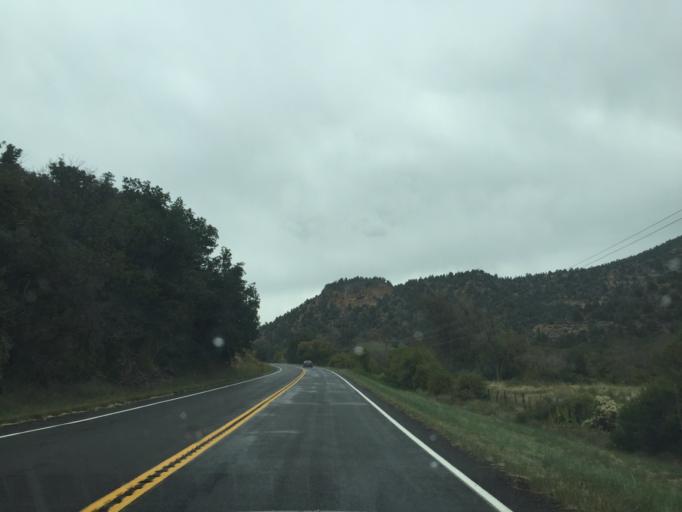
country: US
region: Utah
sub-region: Kane County
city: Kanab
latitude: 37.3491
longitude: -112.5989
